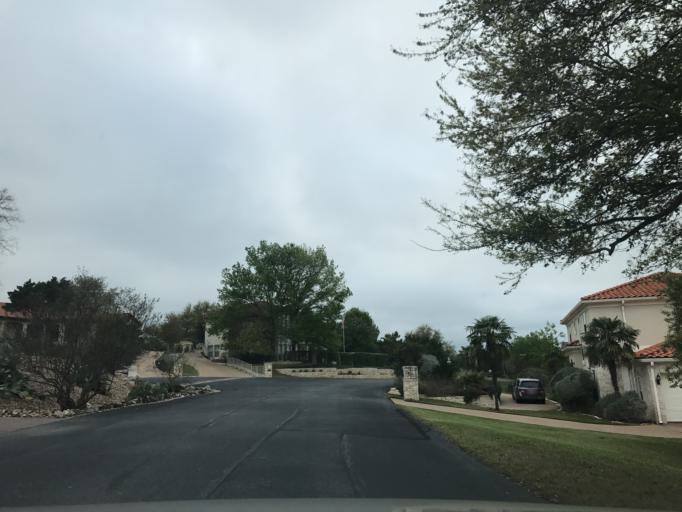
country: US
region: Texas
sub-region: Travis County
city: The Hills
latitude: 30.3410
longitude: -97.9954
